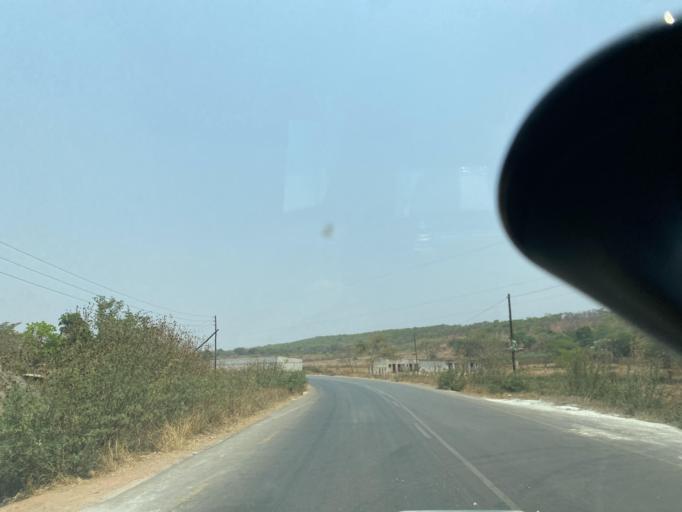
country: ZM
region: Lusaka
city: Lusaka
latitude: -15.5464
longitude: 28.4763
